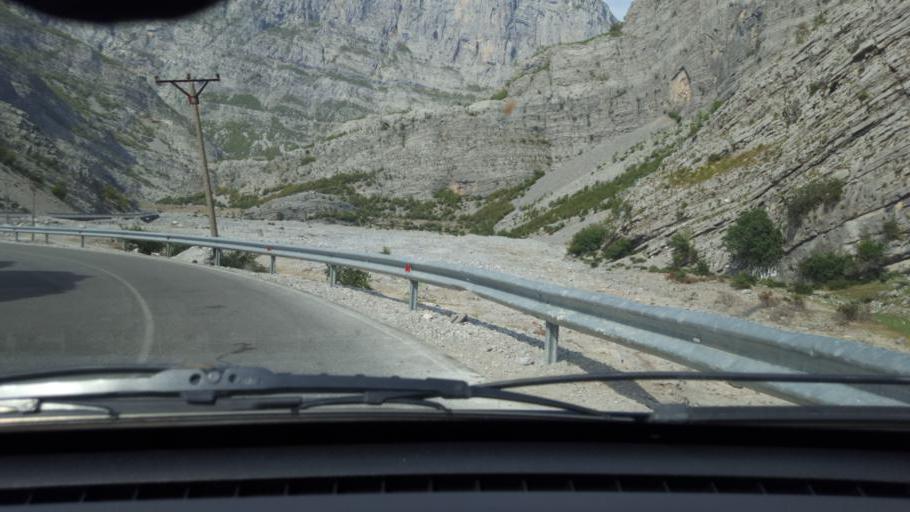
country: AL
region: Shkoder
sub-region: Rrethi i Malesia e Madhe
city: Kastrat
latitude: 42.4867
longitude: 19.5856
